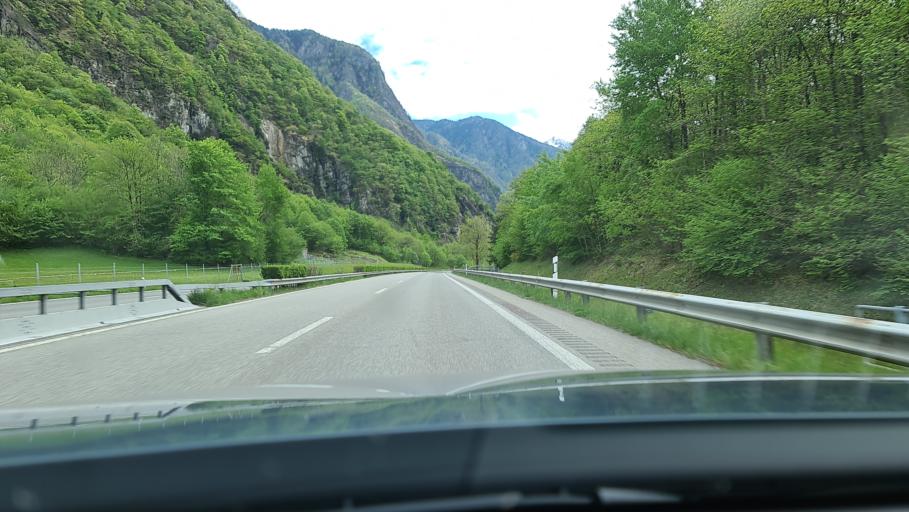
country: CH
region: Grisons
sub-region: Moesa District
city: Santa Maria in Calanca
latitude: 46.2843
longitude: 9.1798
